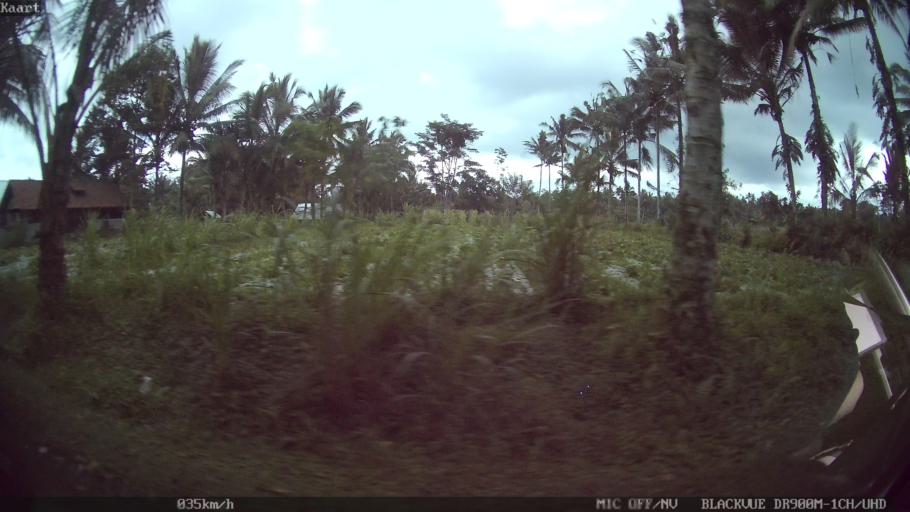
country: ID
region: Bali
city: Banjar Wangsian
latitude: -8.4430
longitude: 115.4254
